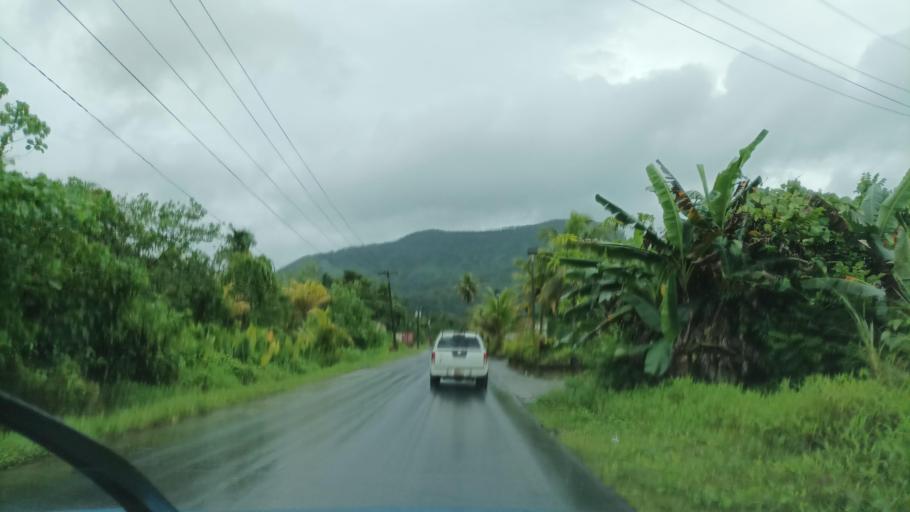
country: FM
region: Pohnpei
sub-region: Sokehs Municipality
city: Palikir - National Government Center
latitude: 6.9418
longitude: 158.1840
